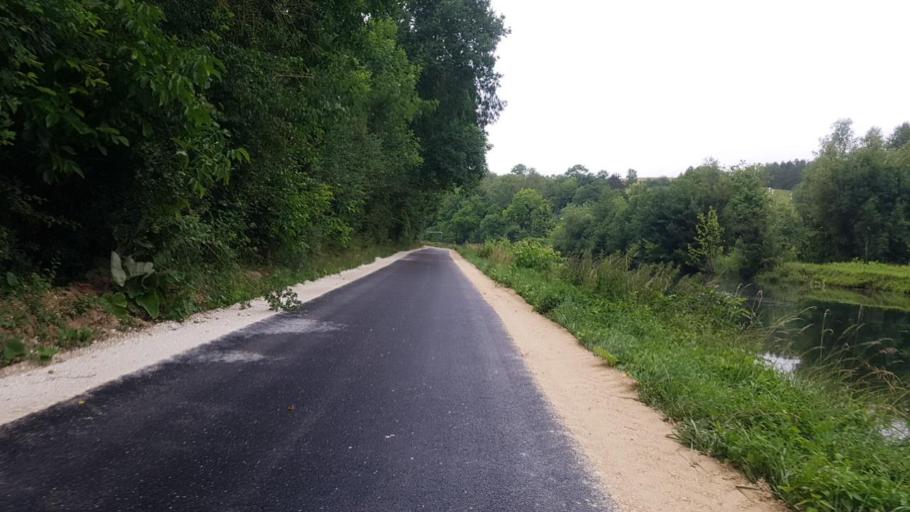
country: FR
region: Champagne-Ardenne
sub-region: Departement de la Marne
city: Vitry-le-Francois
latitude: 48.7919
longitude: 4.5329
